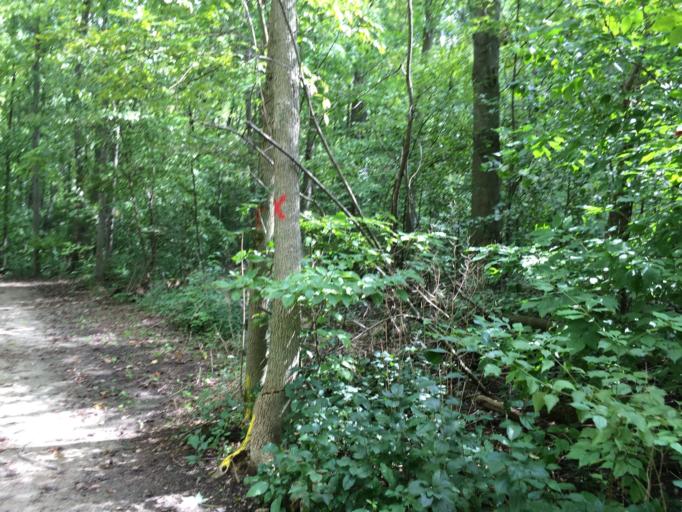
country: CA
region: Ontario
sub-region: Wellington County
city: Guelph
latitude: 43.5251
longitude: -80.2998
